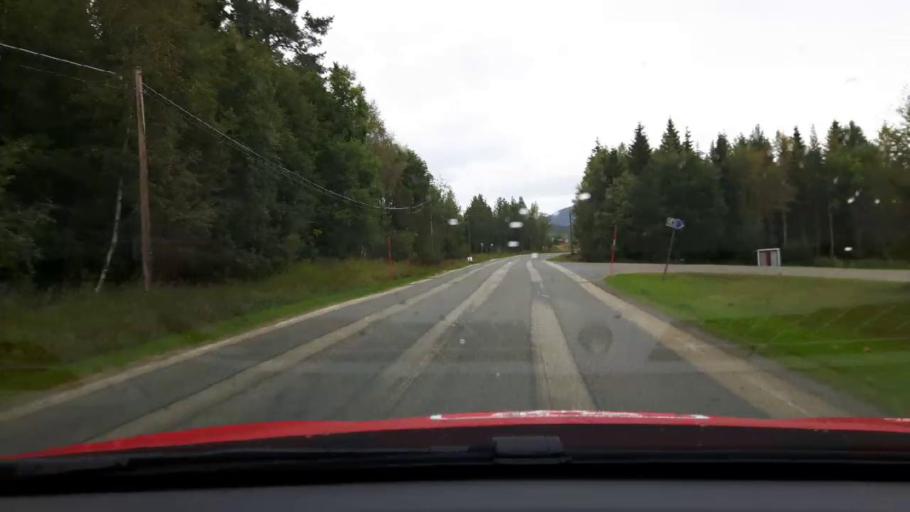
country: SE
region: Jaemtland
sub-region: Bergs Kommun
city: Hoverberg
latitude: 62.7894
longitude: 14.4366
